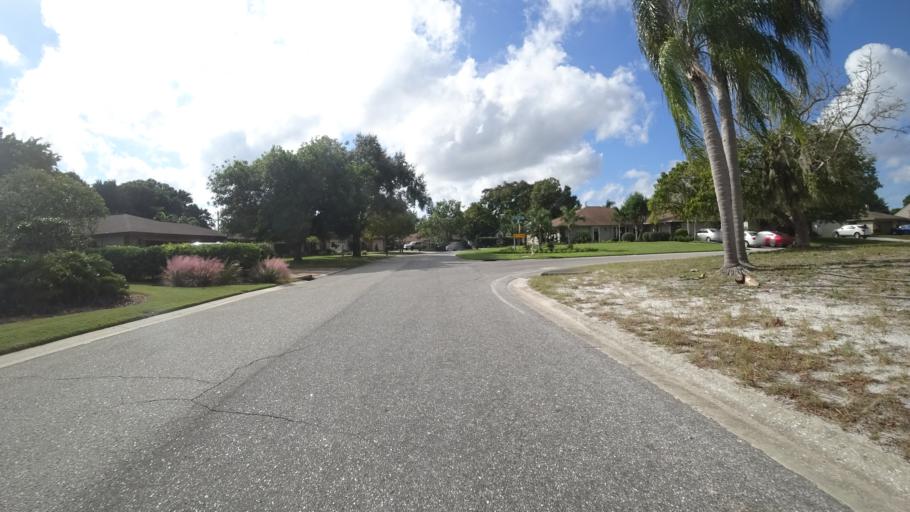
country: US
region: Florida
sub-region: Manatee County
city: West Bradenton
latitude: 27.5008
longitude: -82.6125
